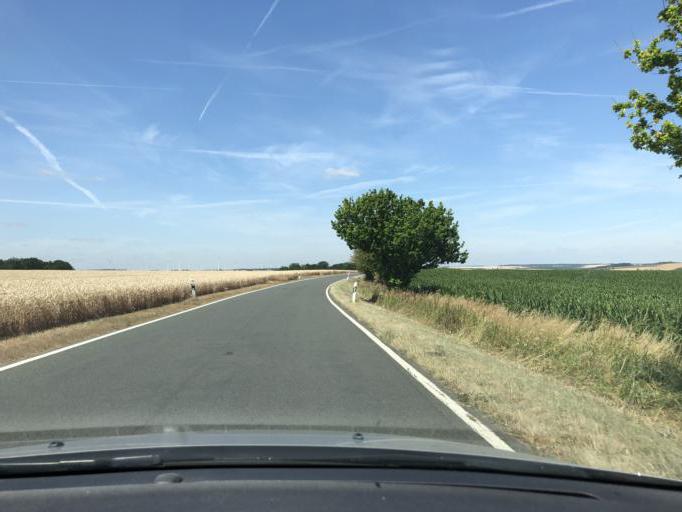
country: DE
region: Saxony-Anhalt
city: Osterfeld
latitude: 51.0627
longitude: 11.8826
